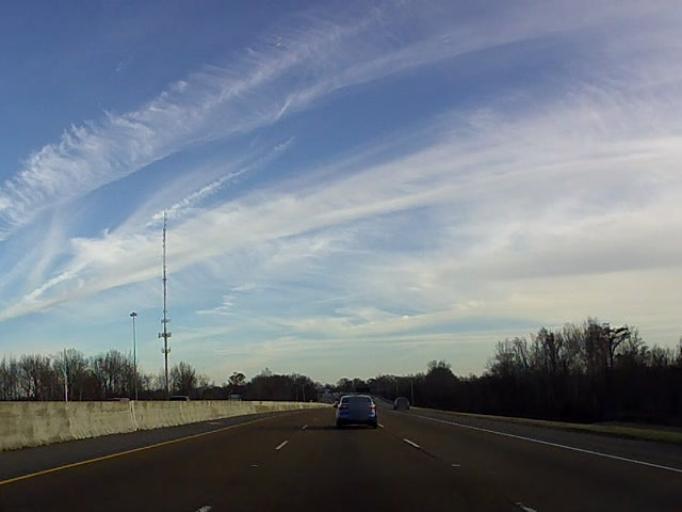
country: US
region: Tennessee
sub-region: Shelby County
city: Germantown
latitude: 35.0737
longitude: -89.8595
